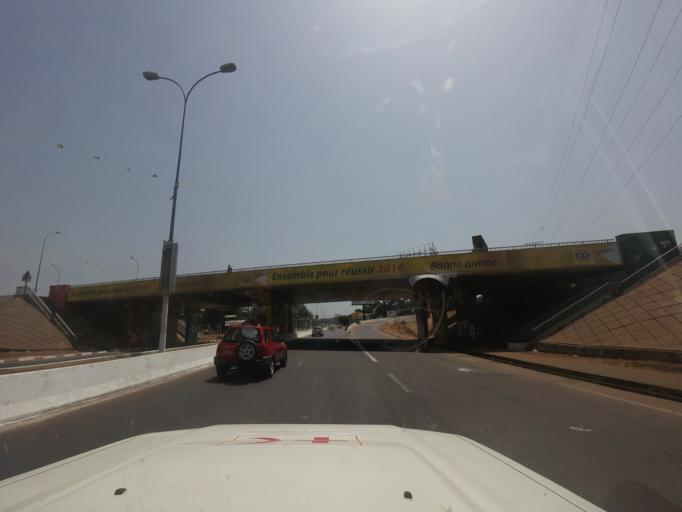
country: GN
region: Conakry
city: Camayenne
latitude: 9.5257
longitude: -13.6881
